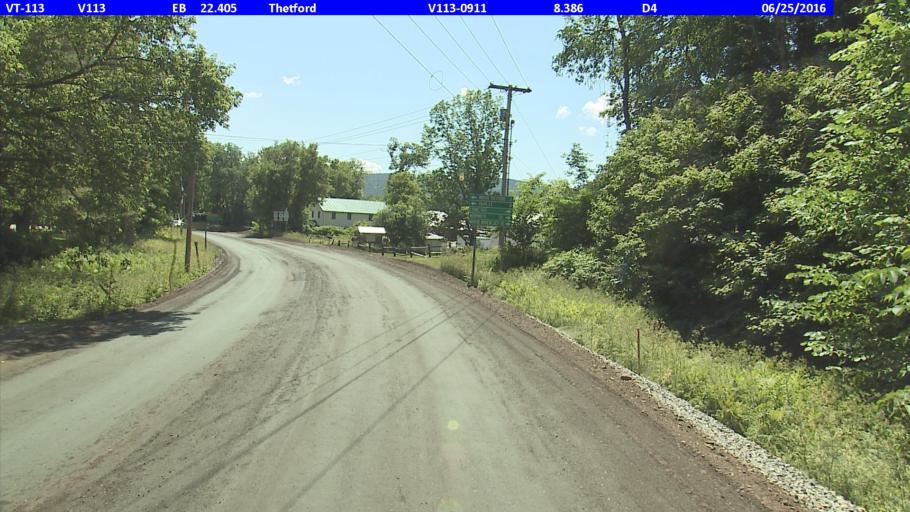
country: US
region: New Hampshire
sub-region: Grafton County
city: Lyme
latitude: 43.8128
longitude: -72.1913
